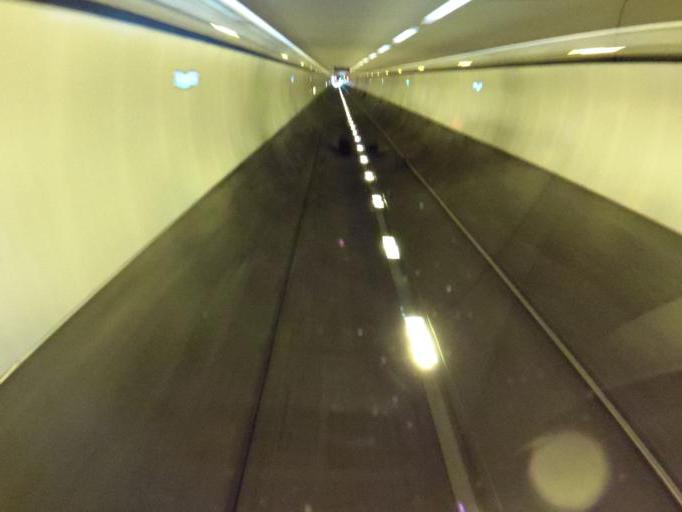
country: IT
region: Trentino-Alto Adige
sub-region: Bolzano
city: Bolzano
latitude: 46.4900
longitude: 11.3508
